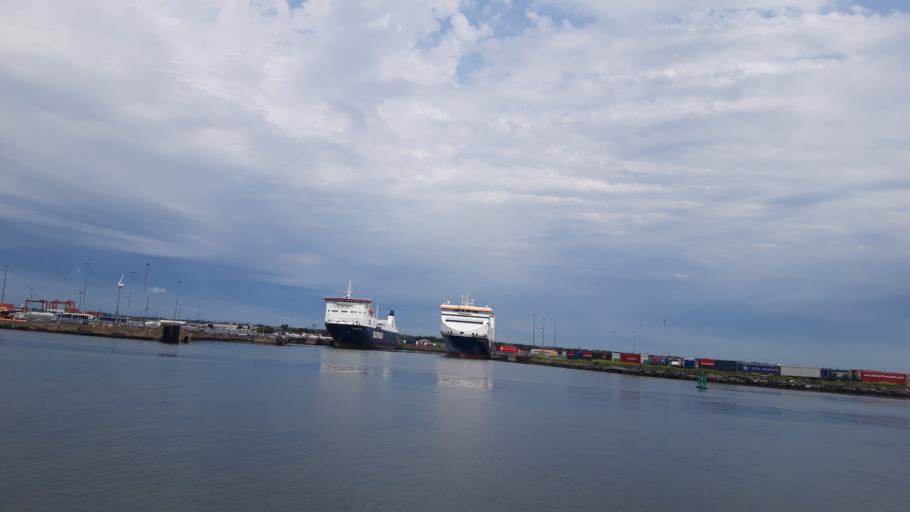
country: IE
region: Leinster
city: Sandymount
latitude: 53.3432
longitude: -6.1914
